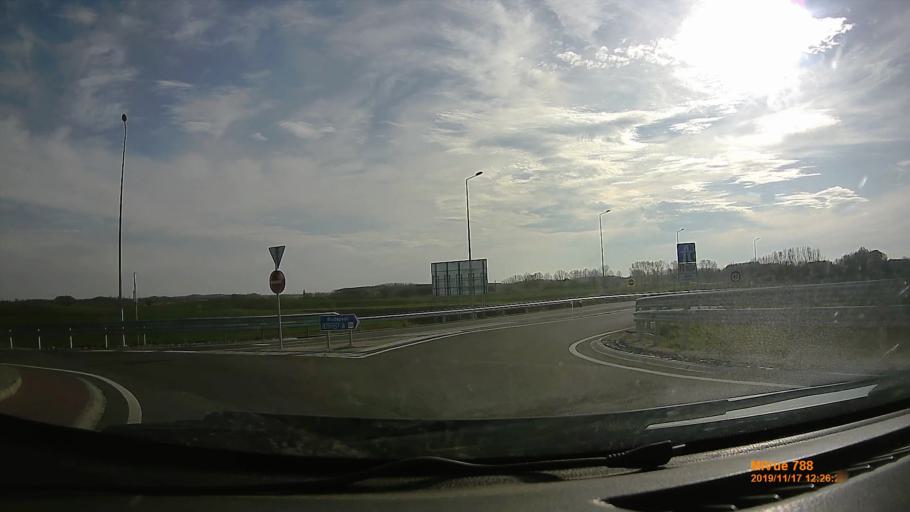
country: HU
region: Bacs-Kiskun
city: Kecskemet
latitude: 46.9326
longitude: 19.6195
